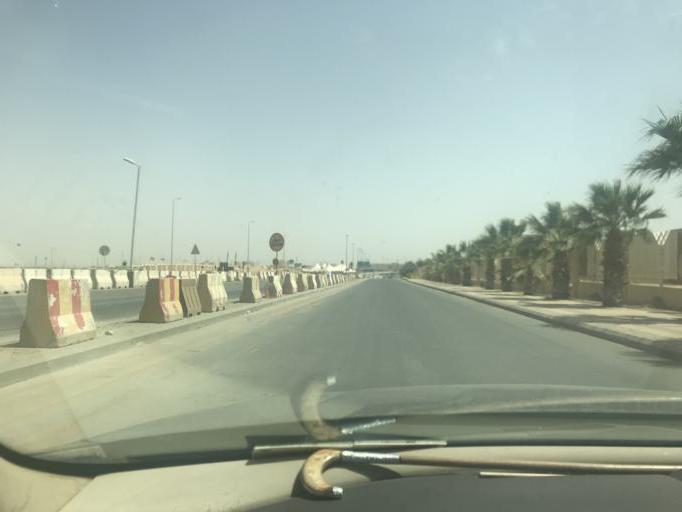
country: SA
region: Ar Riyad
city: Riyadh
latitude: 24.8275
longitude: 46.6956
